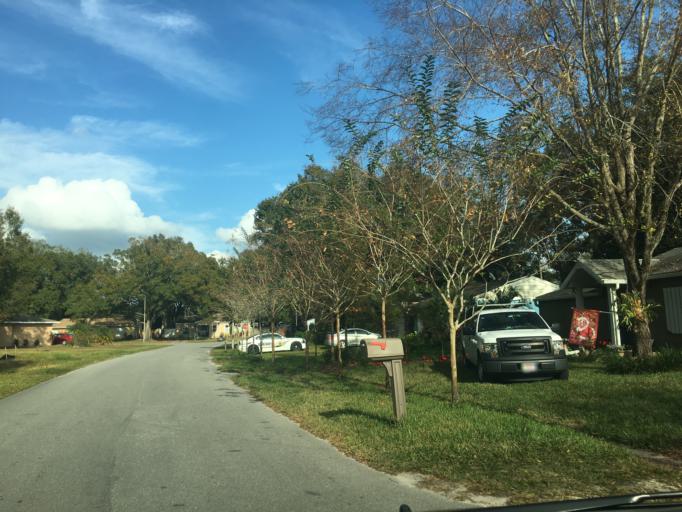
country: US
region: Florida
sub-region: Hillsborough County
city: Egypt Lake-Leto
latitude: 27.9924
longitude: -82.4736
